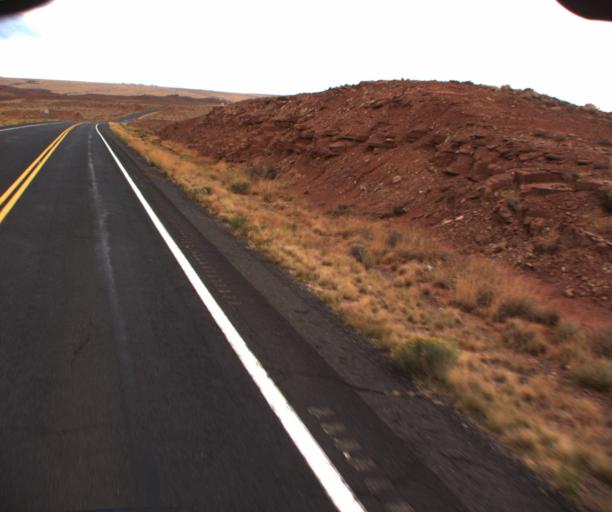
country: US
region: Arizona
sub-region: Coconino County
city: Tuba City
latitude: 35.7930
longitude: -111.4489
